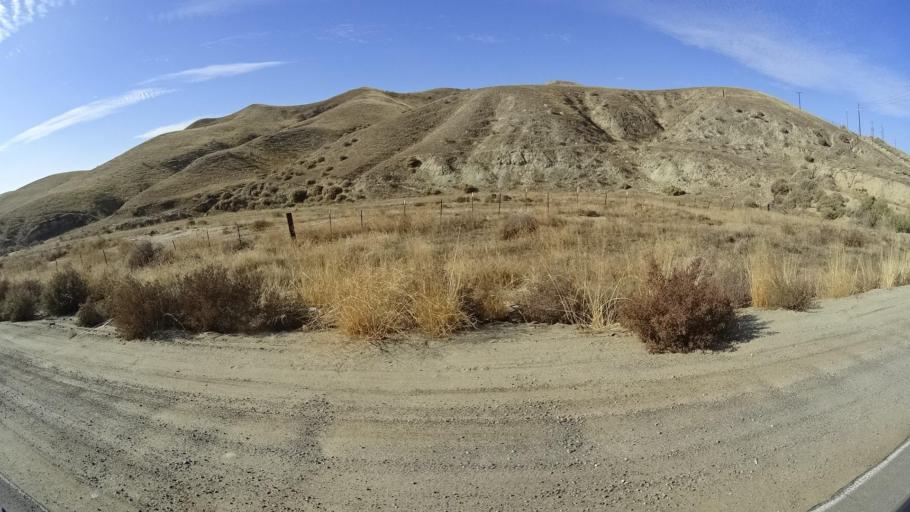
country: US
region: California
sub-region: Kern County
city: Oildale
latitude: 35.5372
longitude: -118.9596
